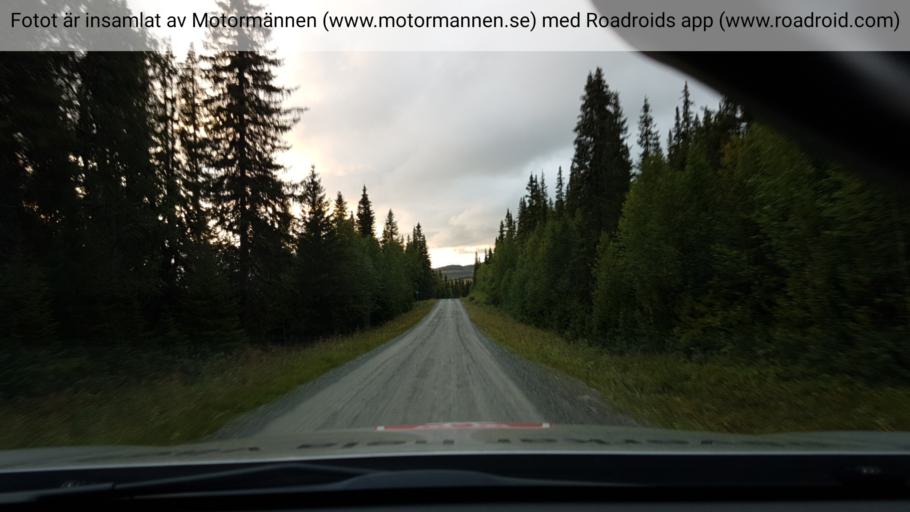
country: SE
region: Vaesterbotten
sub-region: Vilhelmina Kommun
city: Sjoberg
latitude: 65.5424
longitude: 15.4252
